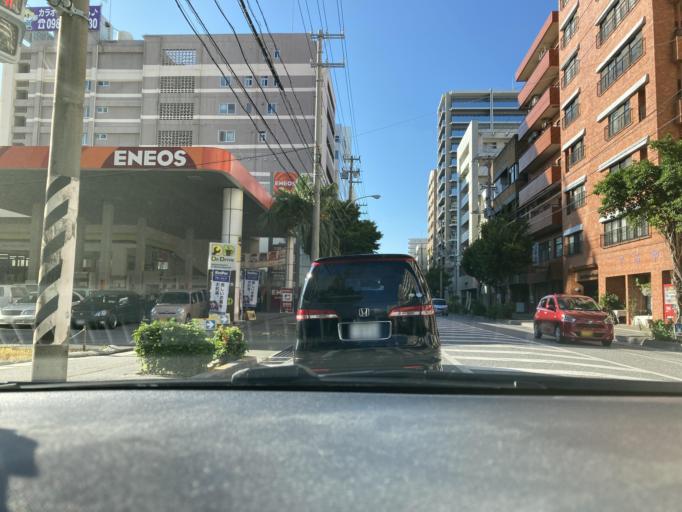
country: JP
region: Okinawa
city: Naha-shi
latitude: 26.2214
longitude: 127.6886
